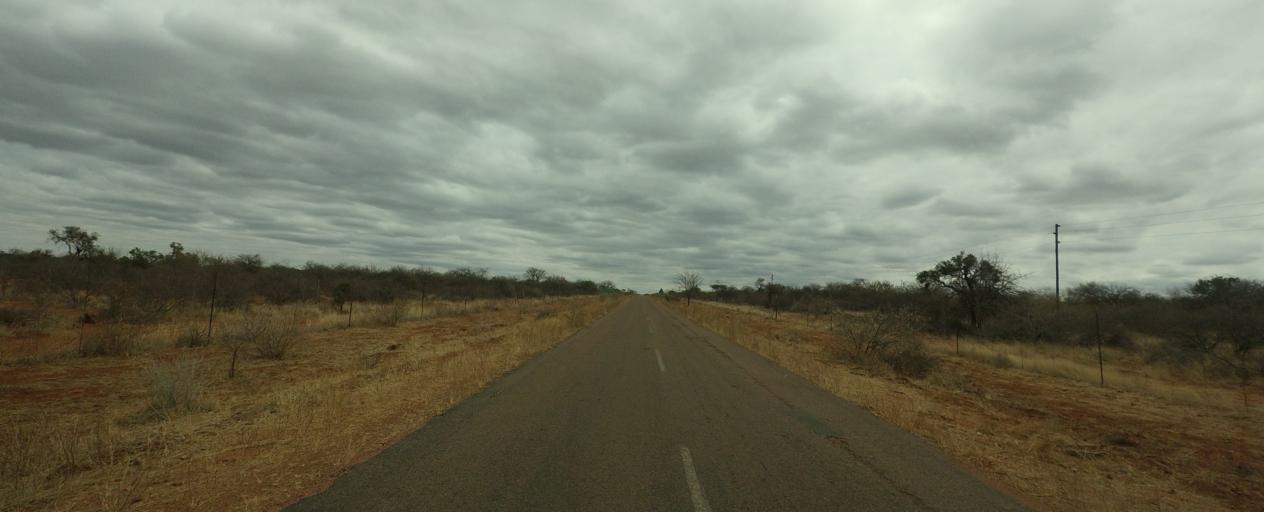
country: BW
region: Central
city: Mathathane
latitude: -22.7392
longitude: 28.4670
